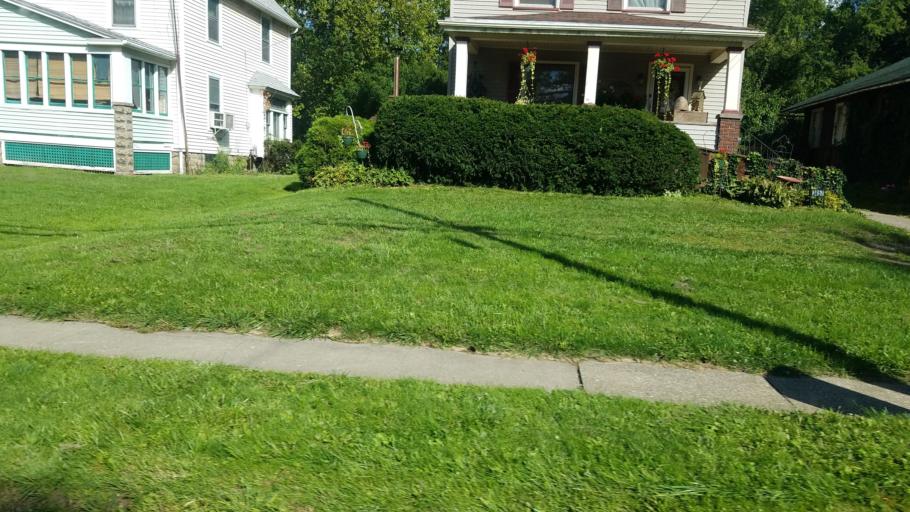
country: US
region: Ohio
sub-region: Trumbull County
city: Mineral Ridge
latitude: 41.1486
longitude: -80.7688
